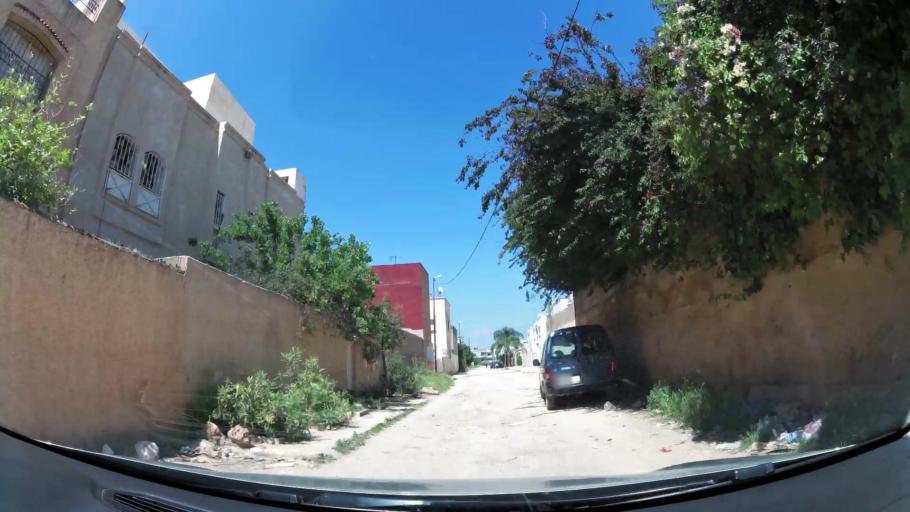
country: MA
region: Fes-Boulemane
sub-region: Fes
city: Fes
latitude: 34.0166
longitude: -5.0246
